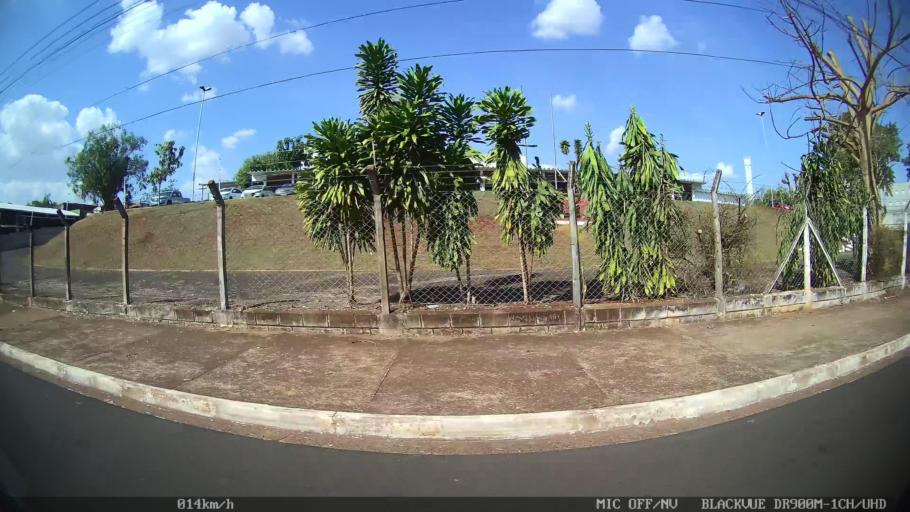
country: BR
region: Sao Paulo
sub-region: Ribeirao Preto
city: Ribeirao Preto
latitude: -21.1839
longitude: -47.8416
